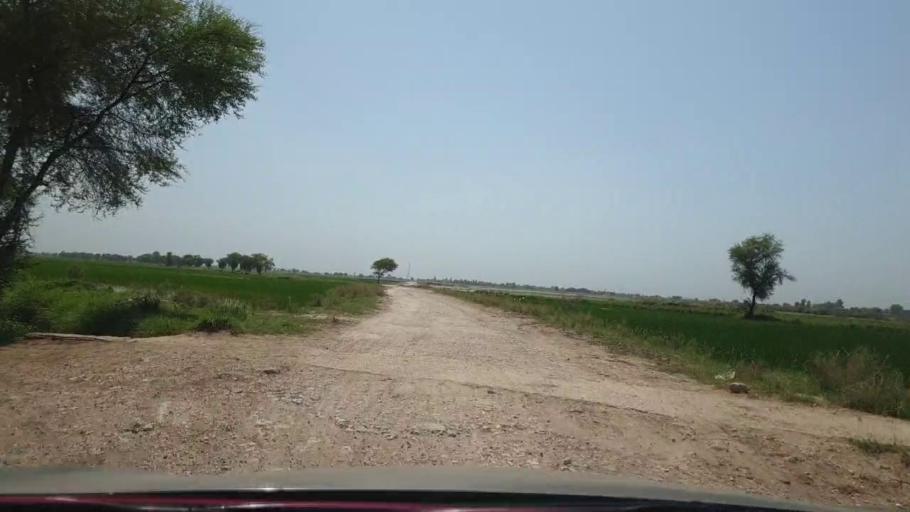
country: PK
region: Sindh
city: Kambar
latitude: 27.5653
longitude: 67.8820
